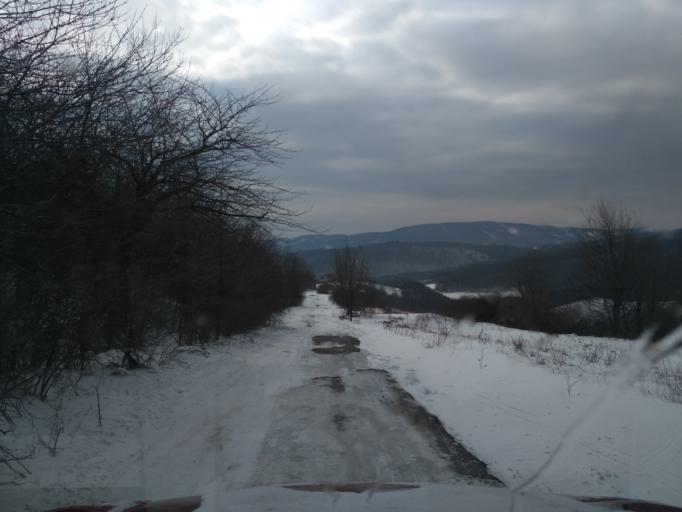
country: SK
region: Kosicky
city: Kosice
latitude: 48.7530
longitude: 21.1243
